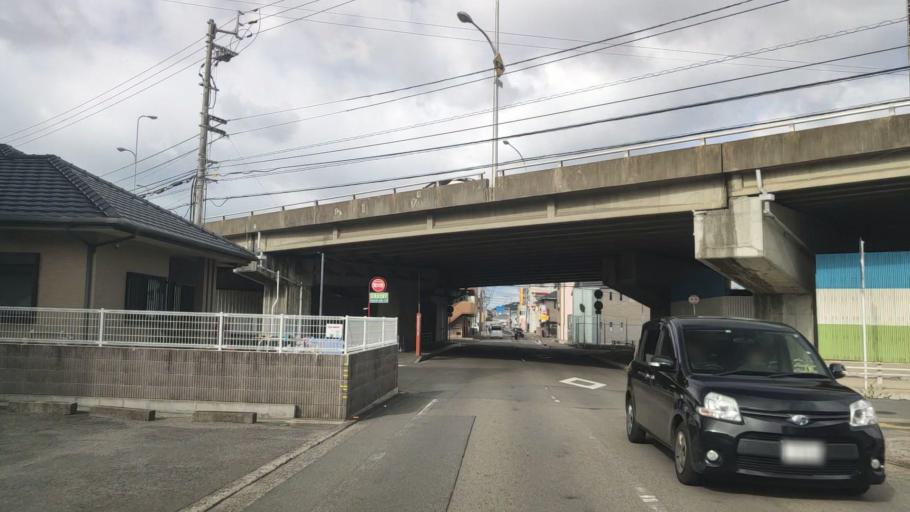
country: JP
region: Ehime
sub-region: Shikoku-chuo Shi
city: Matsuyama
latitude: 33.8215
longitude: 132.7591
